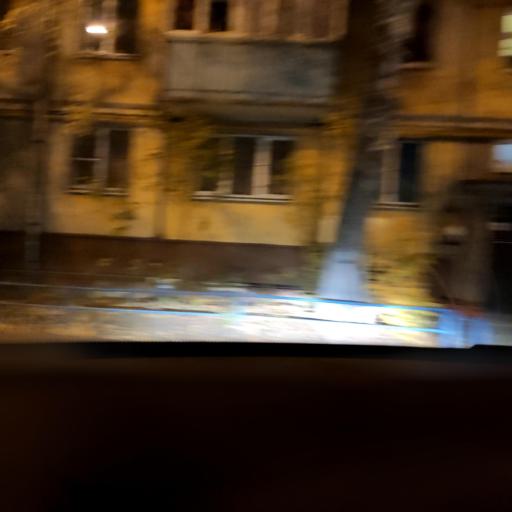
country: RU
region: Samara
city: Samara
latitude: 53.1960
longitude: 50.1965
